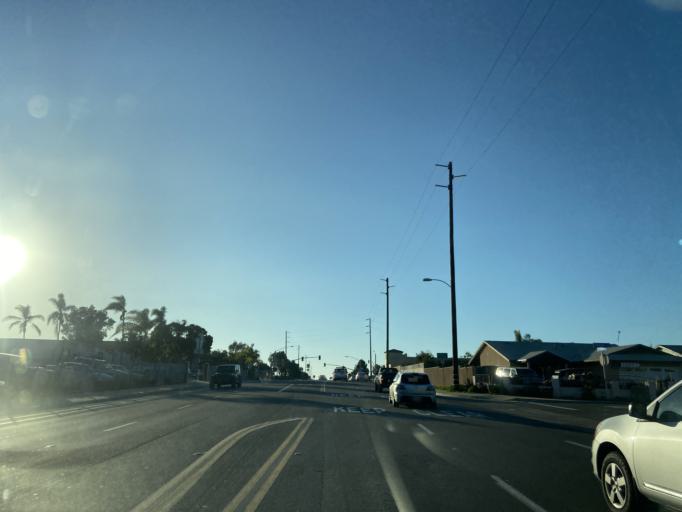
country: US
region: California
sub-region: San Diego County
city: Imperial Beach
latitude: 32.5765
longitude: -117.0908
